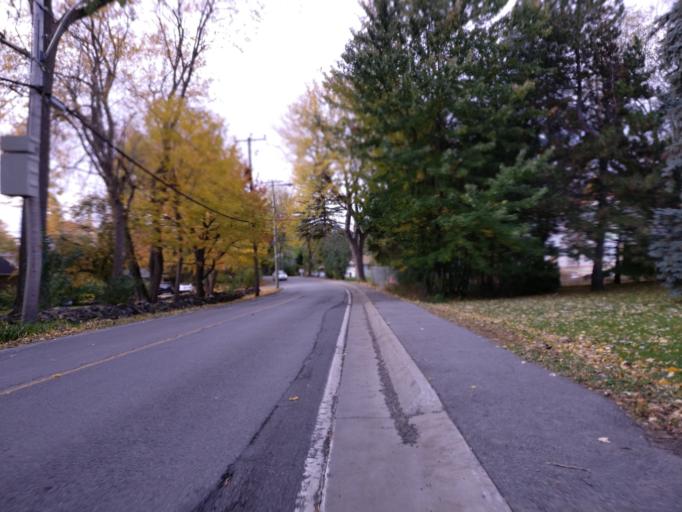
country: CA
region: Quebec
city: Baie-D'Urfe
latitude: 45.4054
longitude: -73.9287
